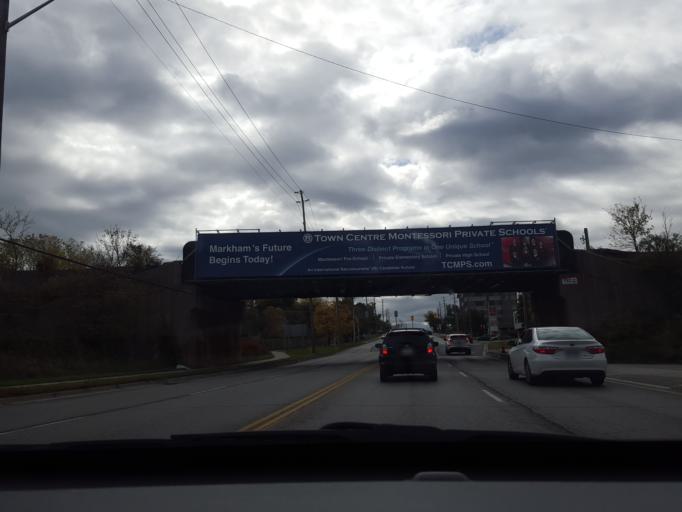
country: CA
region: Ontario
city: Markham
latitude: 43.8476
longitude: -79.3061
